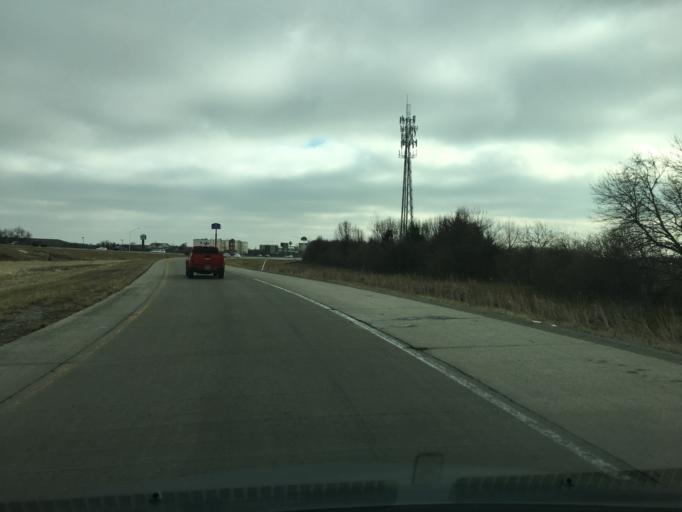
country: US
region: Indiana
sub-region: Tippecanoe County
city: Lafayette
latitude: 40.4163
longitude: -86.8214
